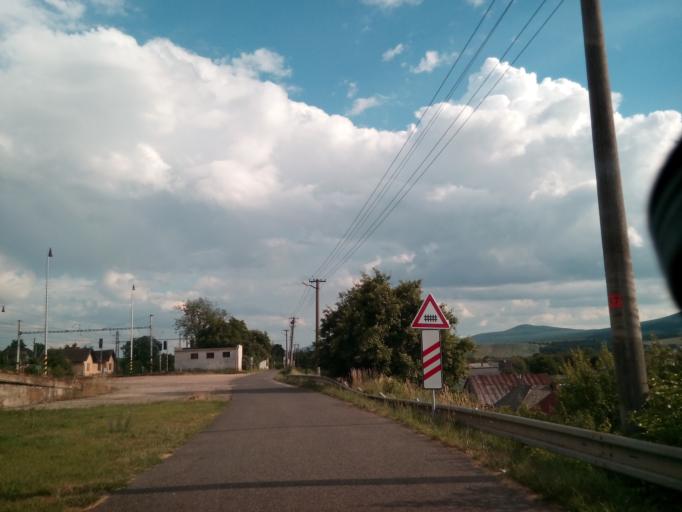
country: SK
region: Kosicky
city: Secovce
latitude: 48.5808
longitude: 21.5788
